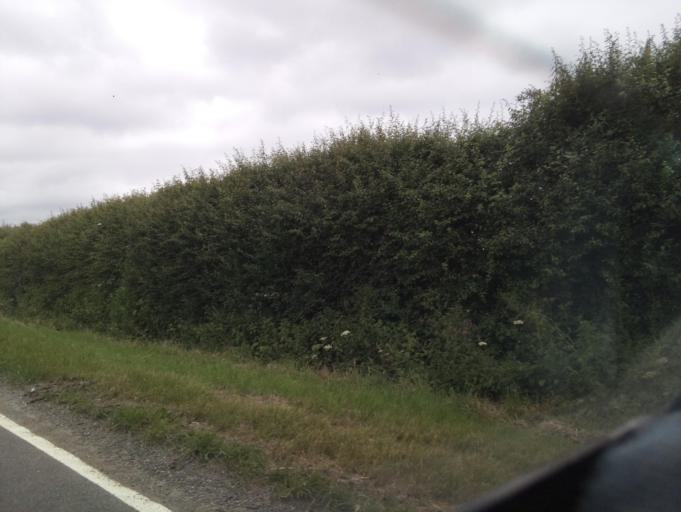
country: GB
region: England
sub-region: Leicestershire
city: Grimston
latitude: 52.7862
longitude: -1.0079
